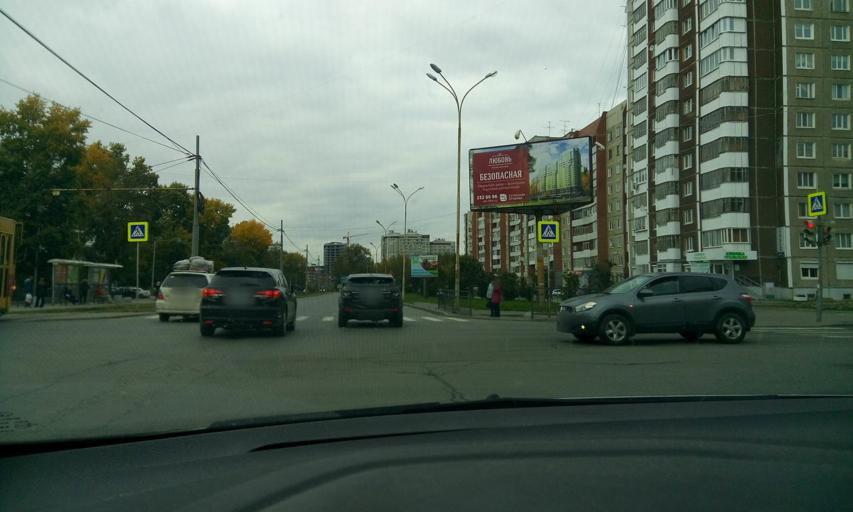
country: RU
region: Sverdlovsk
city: Yekaterinburg
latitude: 56.8578
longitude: 60.6308
